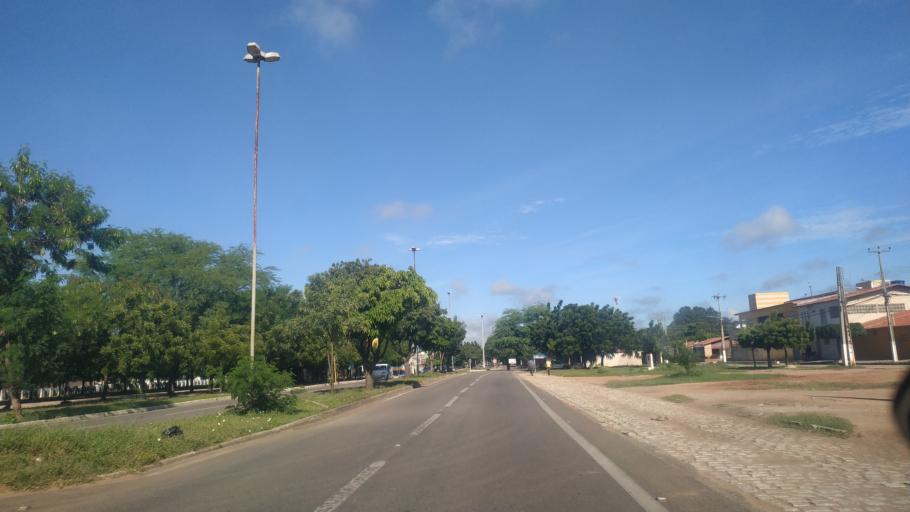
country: BR
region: Rio Grande do Norte
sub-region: Mossoro
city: Mossoro
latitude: -5.1916
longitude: -37.3618
